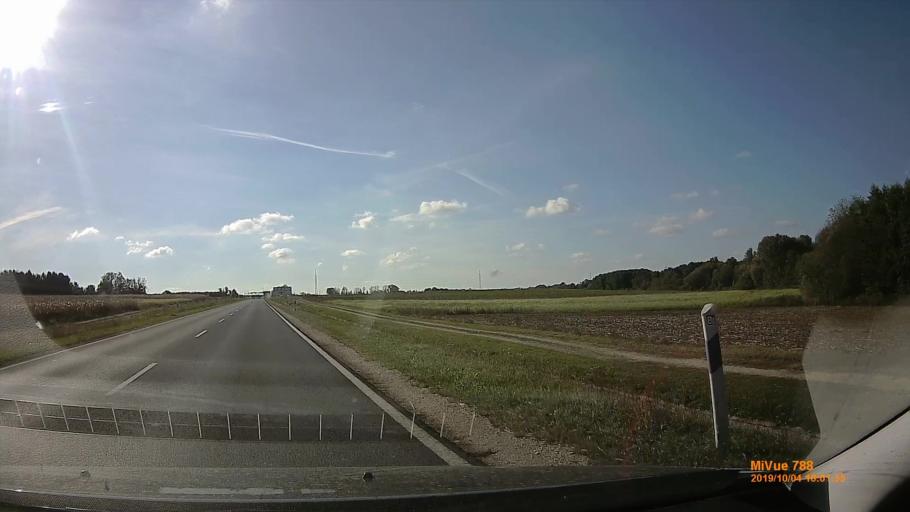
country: HU
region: Somogy
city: Kaposvar
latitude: 46.4052
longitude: 17.7732
